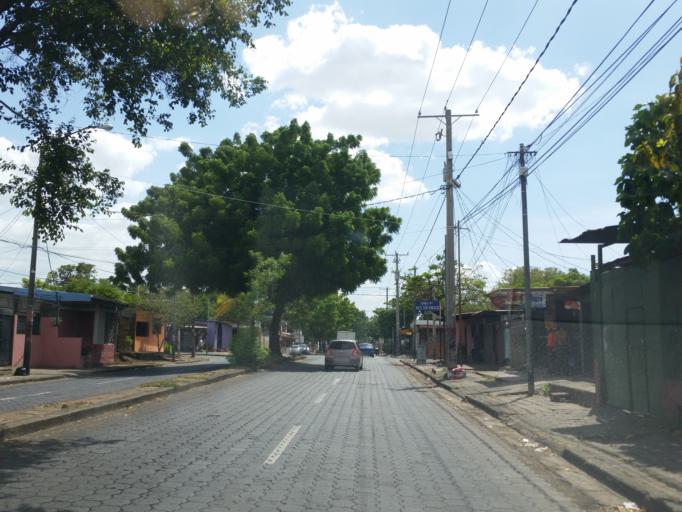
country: NI
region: Managua
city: Managua
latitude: 12.1463
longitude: -86.2434
